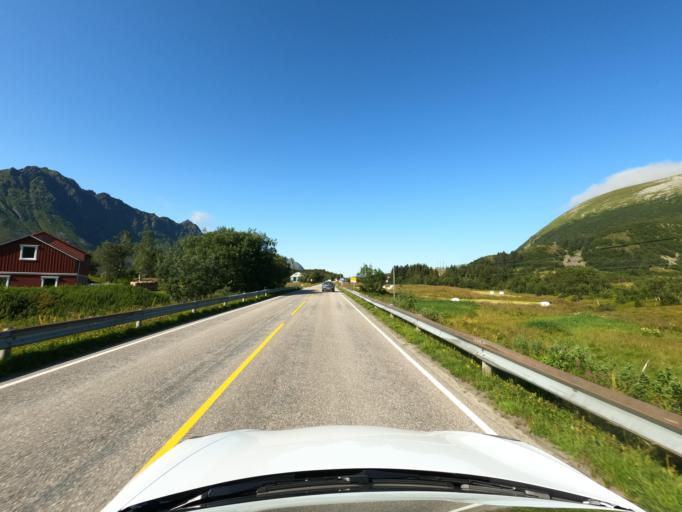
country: NO
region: Nordland
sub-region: Vagan
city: Kabelvag
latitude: 68.2532
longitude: 14.2753
